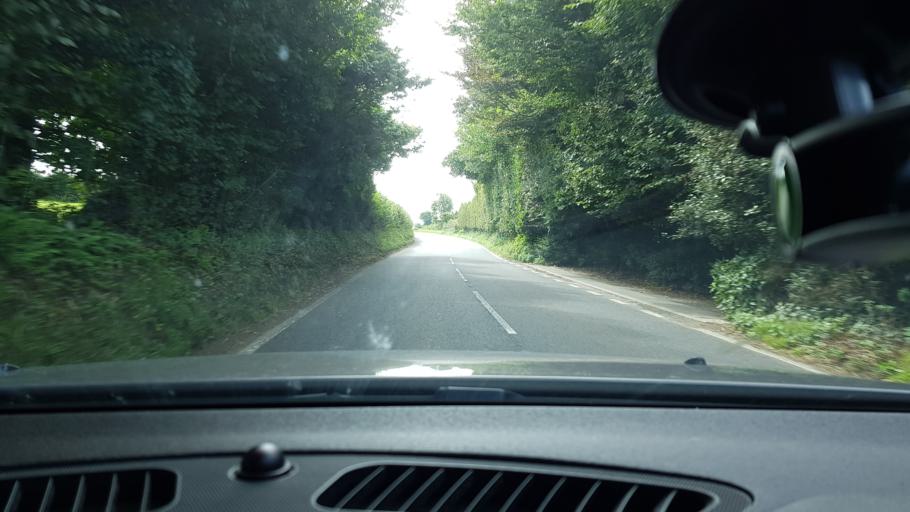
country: GB
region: England
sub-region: Cornwall
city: Camelford
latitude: 50.6023
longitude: -4.6967
